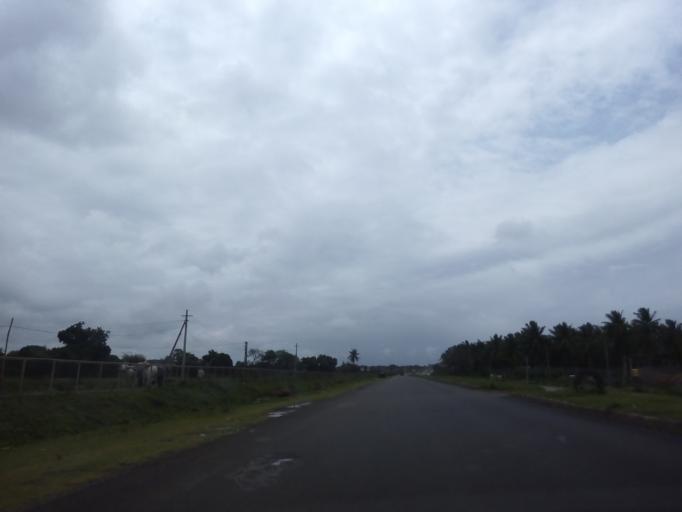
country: IN
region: Karnataka
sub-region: Haveri
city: Byadgi
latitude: 14.7169
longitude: 75.4851
